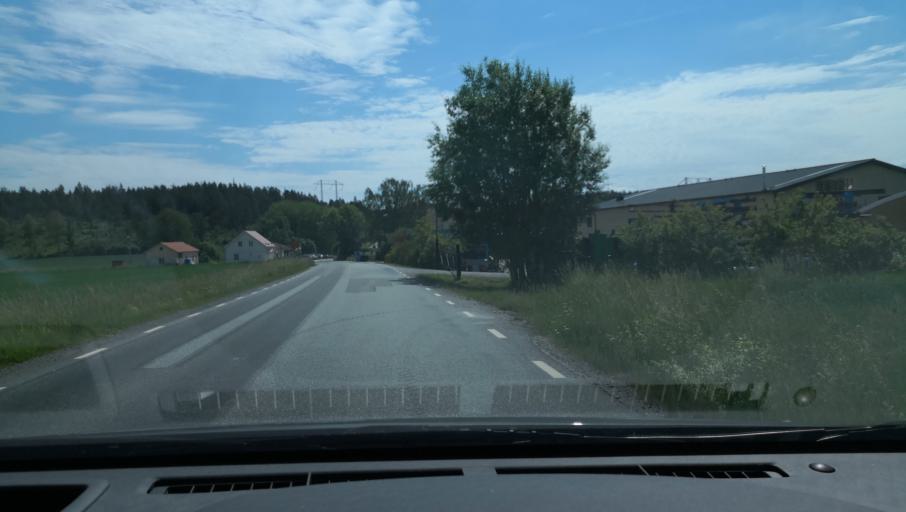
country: SE
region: Uppsala
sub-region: Habo Kommun
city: Balsta
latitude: 59.6642
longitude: 17.4484
